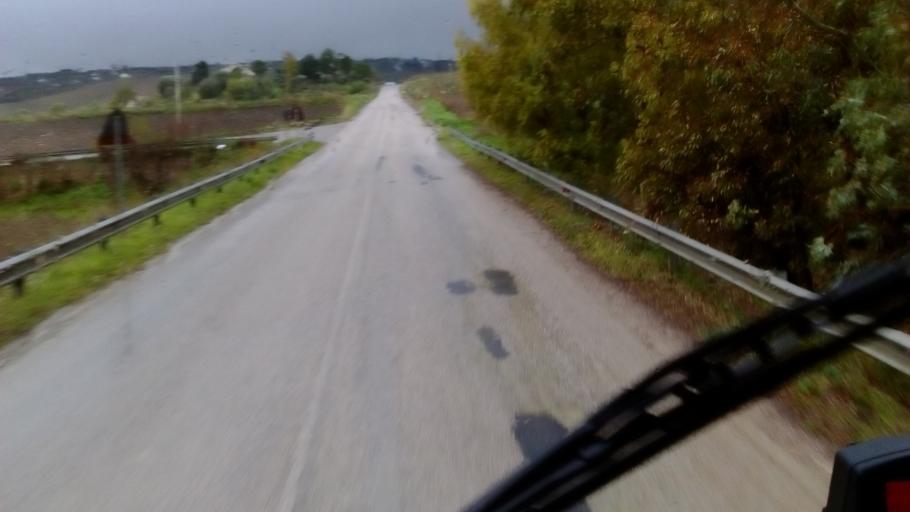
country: IT
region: Sicily
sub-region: Enna
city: Pietraperzia
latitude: 37.4492
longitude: 14.1775
